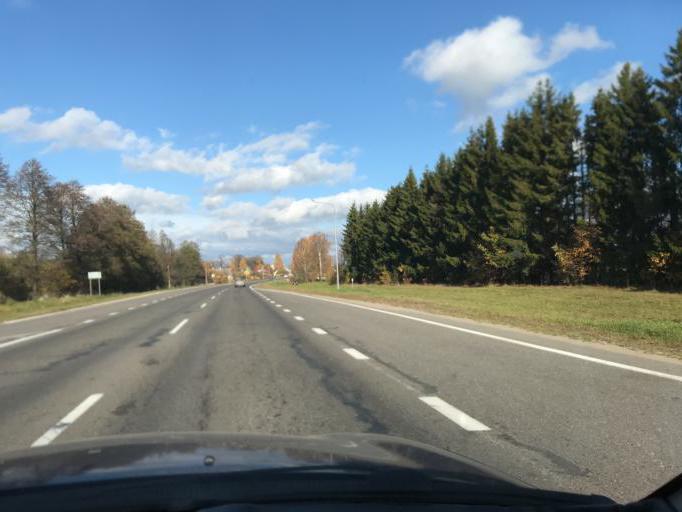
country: LT
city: Salcininkai
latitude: 54.2364
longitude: 25.3559
